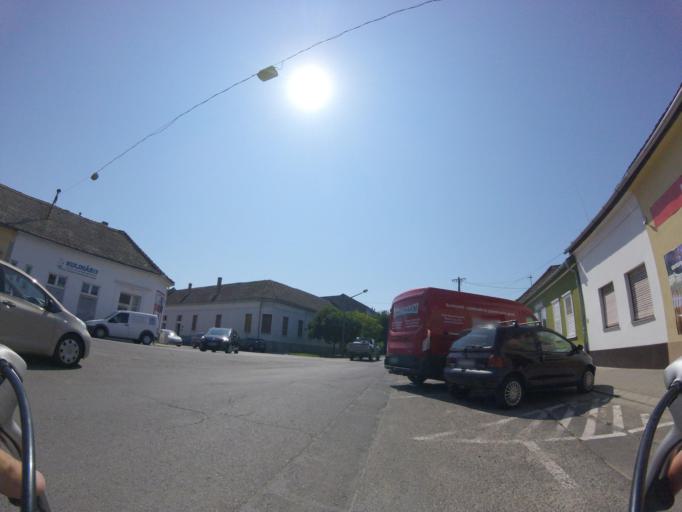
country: HU
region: Bacs-Kiskun
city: Baja
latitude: 46.1735
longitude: 18.9523
